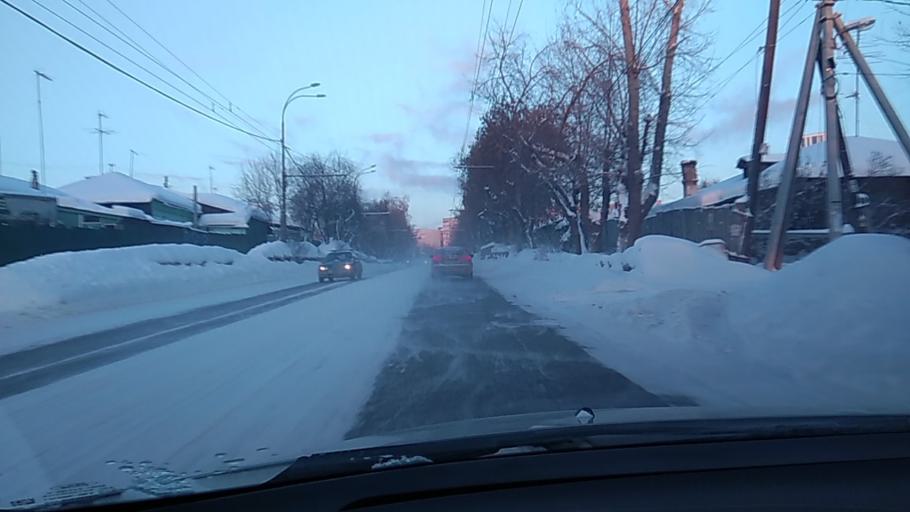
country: RU
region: Sverdlovsk
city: Yekaterinburg
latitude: 56.8042
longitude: 60.5888
